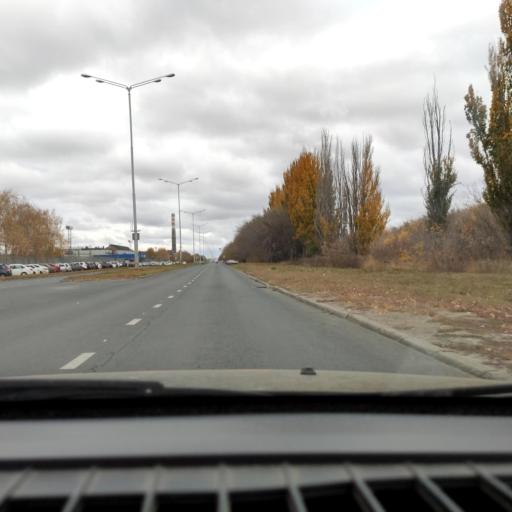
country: RU
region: Samara
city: Tol'yatti
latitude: 53.5686
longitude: 49.2692
